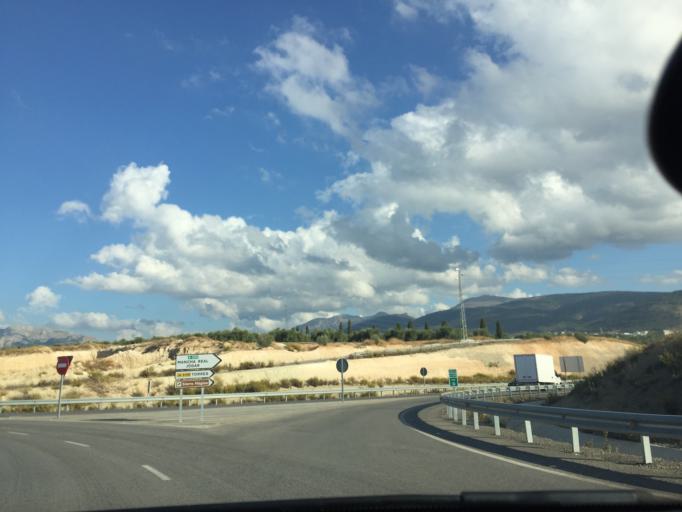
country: ES
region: Andalusia
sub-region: Provincia de Jaen
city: Mancha Real
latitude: 37.8040
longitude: -3.6264
